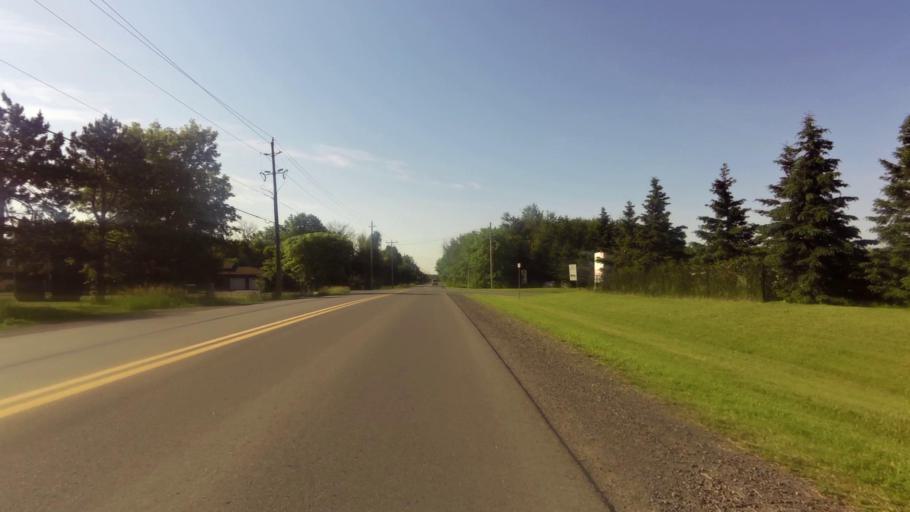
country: CA
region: Ontario
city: Ottawa
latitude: 45.2547
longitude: -75.5662
